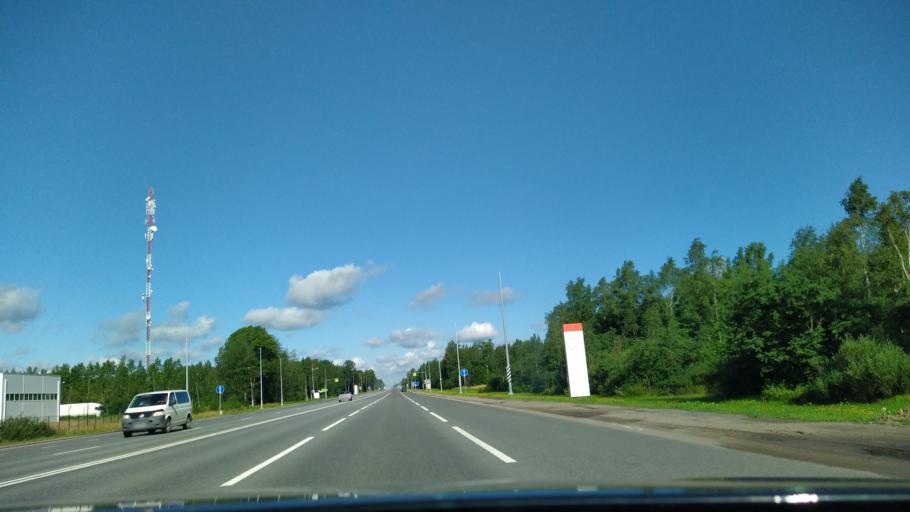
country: RU
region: Leningrad
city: Tosno
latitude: 59.5705
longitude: 30.8234
